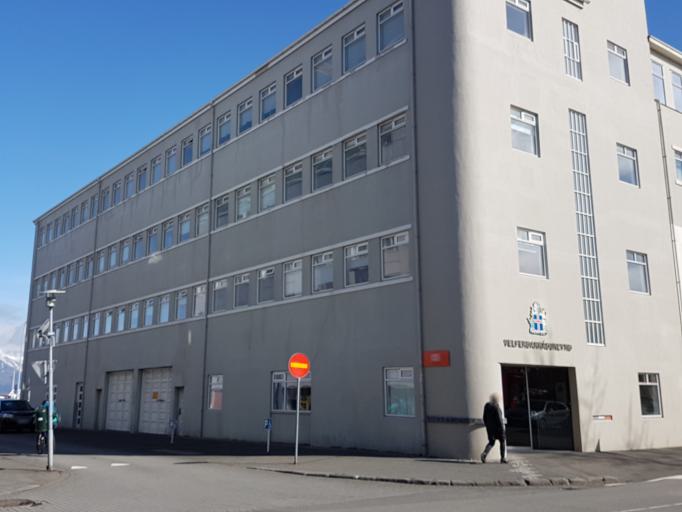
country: IS
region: Capital Region
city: Kopavogur
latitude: 64.1493
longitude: -21.9416
